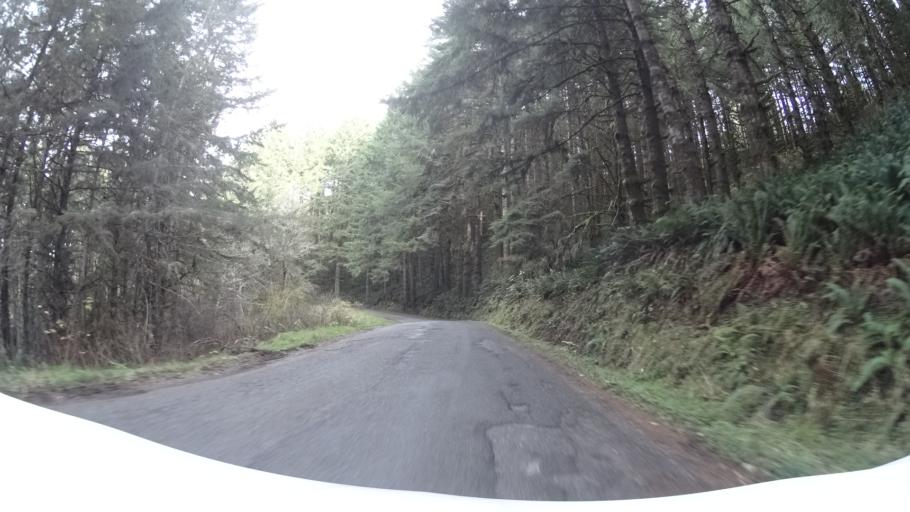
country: US
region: California
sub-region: Humboldt County
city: Ferndale
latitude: 40.5184
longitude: -124.2679
